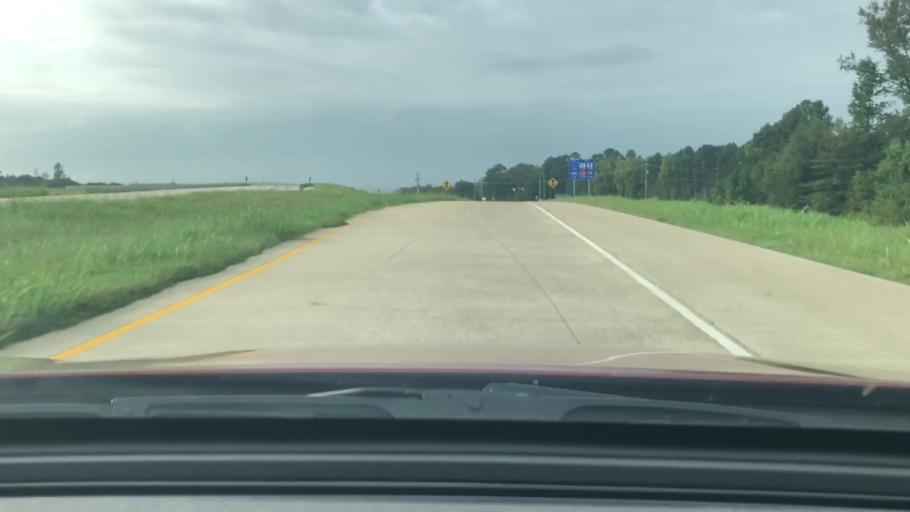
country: US
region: Louisiana
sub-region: Caddo Parish
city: Blanchard
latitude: 32.5995
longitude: -93.8329
